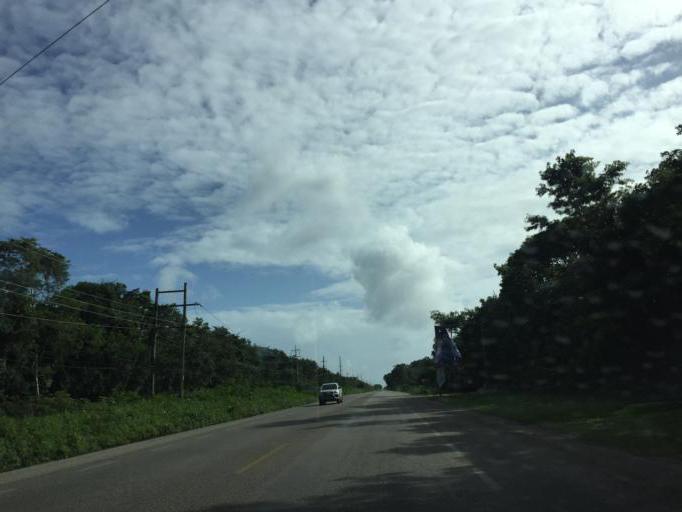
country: MX
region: Quintana Roo
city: Tulum
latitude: 20.2514
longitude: -87.4667
